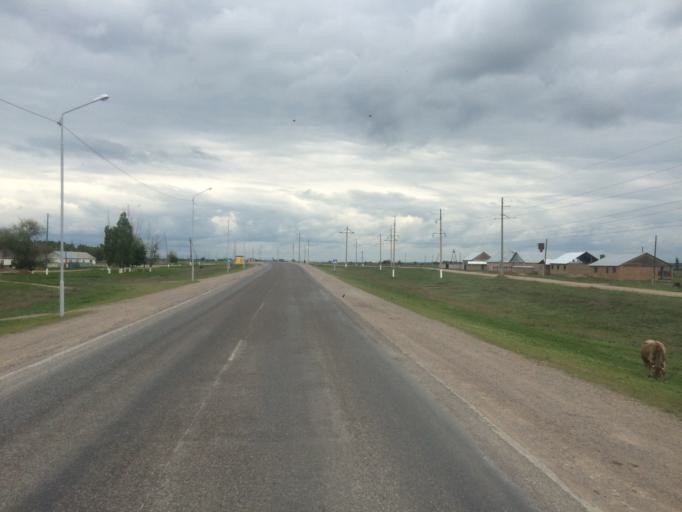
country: KG
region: Chuy
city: Sokuluk
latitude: 43.2474
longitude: 74.2972
